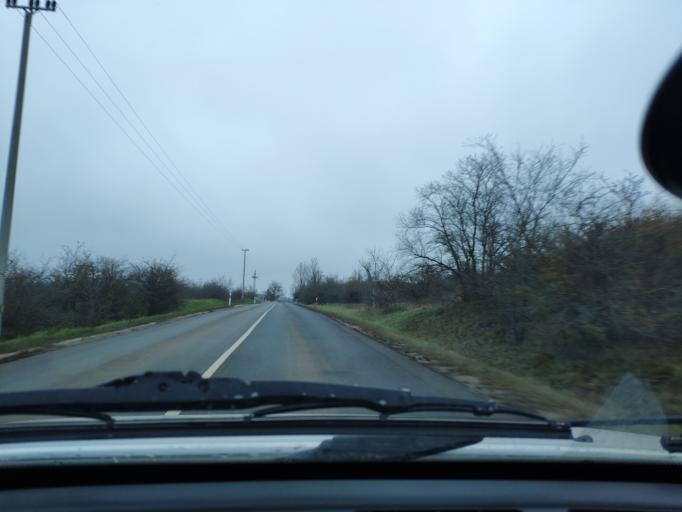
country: HU
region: Pest
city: Soskut
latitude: 47.4157
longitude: 18.8280
